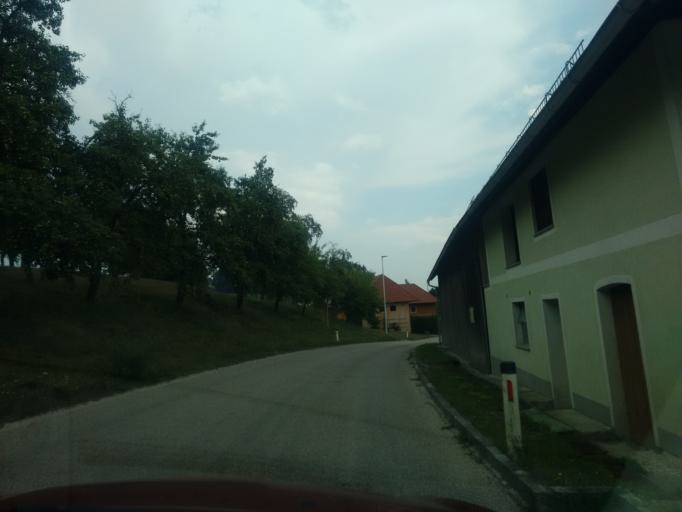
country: AT
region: Upper Austria
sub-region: Politischer Bezirk Grieskirchen
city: Bad Schallerbach
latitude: 48.2469
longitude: 13.9095
